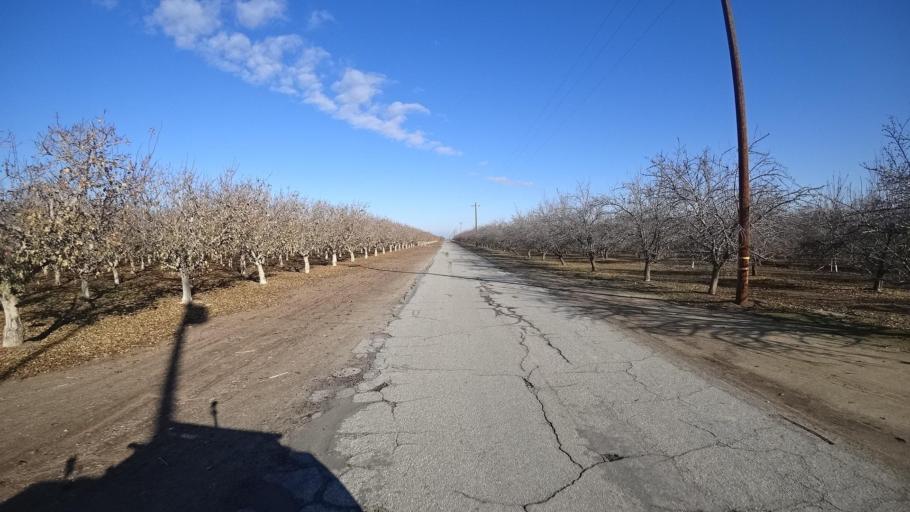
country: US
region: California
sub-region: Kern County
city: McFarland
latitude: 35.6924
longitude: -119.2942
